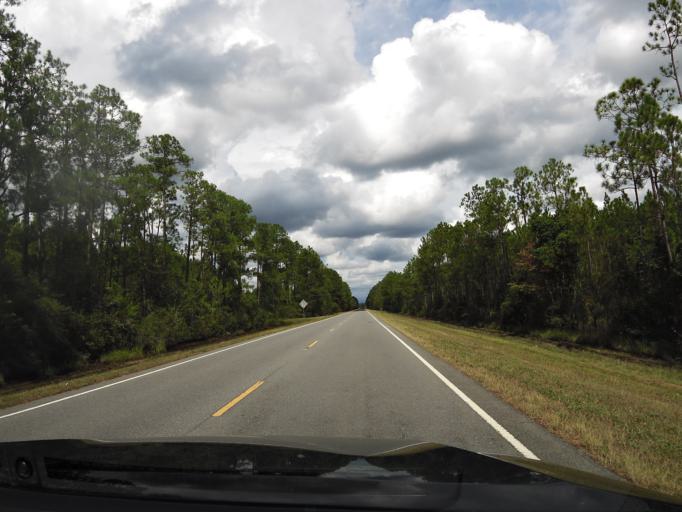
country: US
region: Georgia
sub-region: Brantley County
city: Nahunta
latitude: 31.1318
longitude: -81.9977
